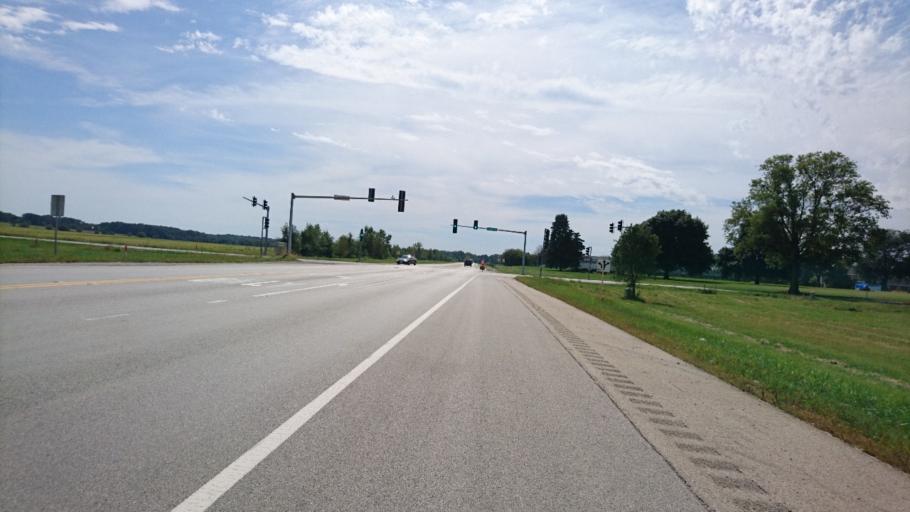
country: US
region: Illinois
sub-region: Will County
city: Wilmington
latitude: 41.3208
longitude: -88.1327
